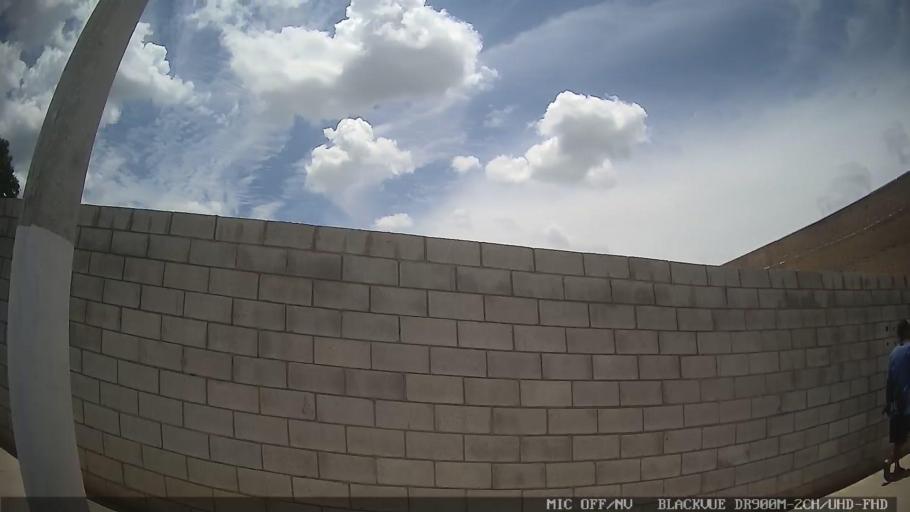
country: BR
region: Sao Paulo
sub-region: Atibaia
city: Atibaia
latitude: -23.1111
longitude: -46.5612
